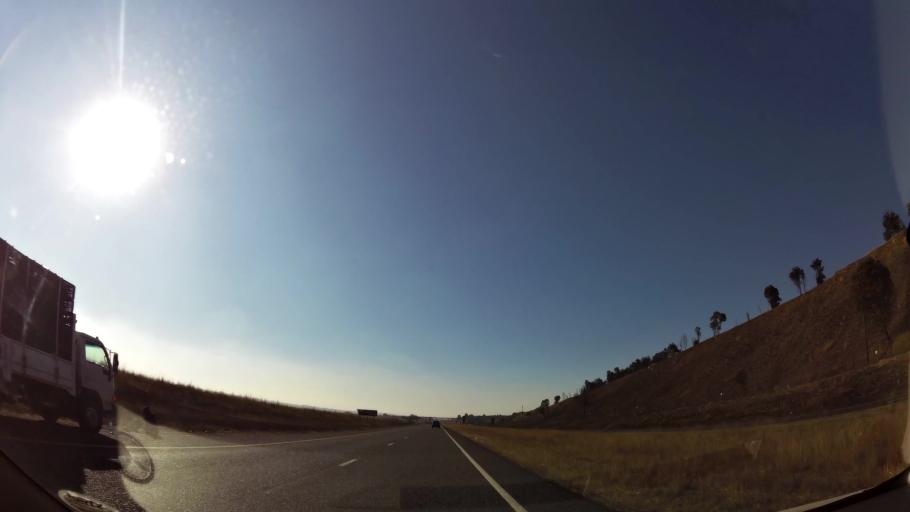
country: ZA
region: Mpumalanga
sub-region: Nkangala District Municipality
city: Witbank
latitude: -26.0210
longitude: 29.0226
